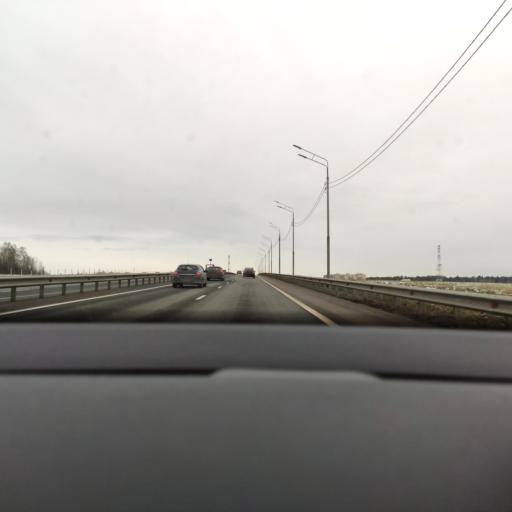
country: RU
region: Moskovskaya
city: Zvenigorod
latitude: 55.6895
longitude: 36.8848
